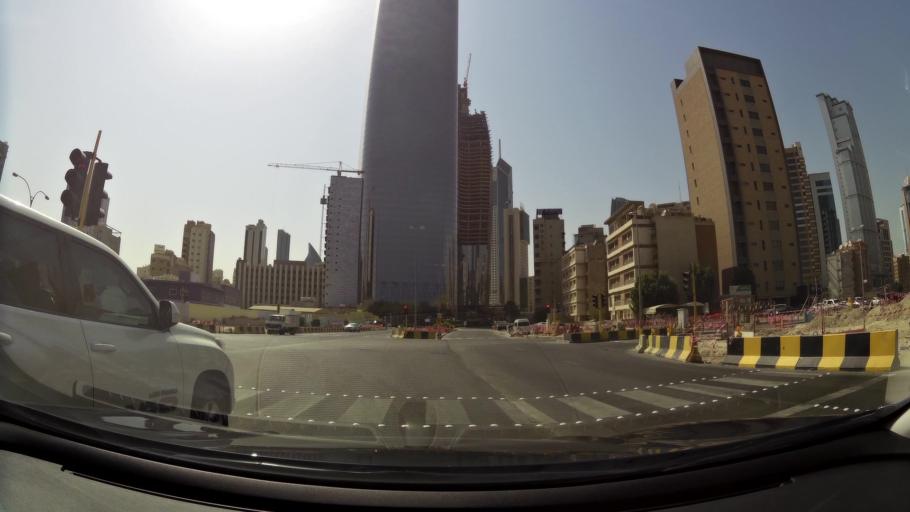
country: KW
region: Al Asimah
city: Ad Dasmah
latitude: 29.3818
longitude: 47.9940
